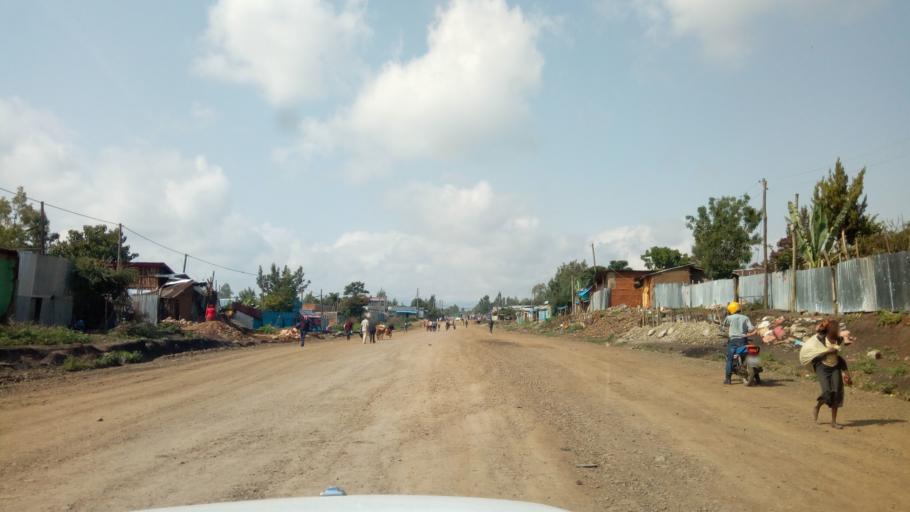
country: ET
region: Oromiya
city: Hagere Hiywet
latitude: 8.9779
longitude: 37.8519
